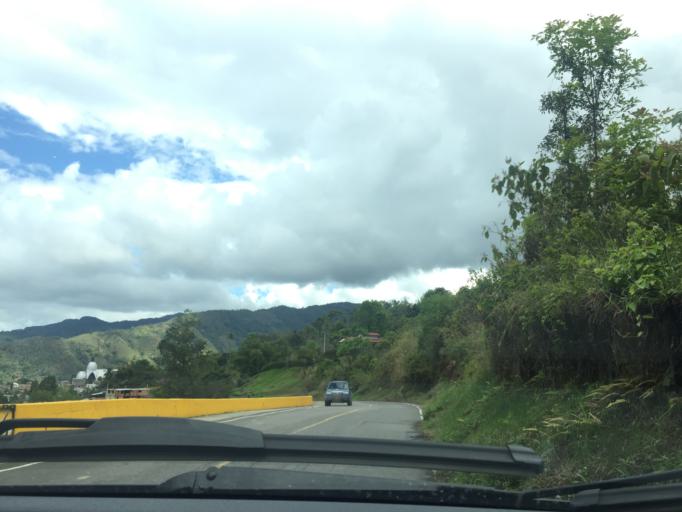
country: CO
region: Cundinamarca
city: Supata
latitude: 5.0559
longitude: -74.2348
